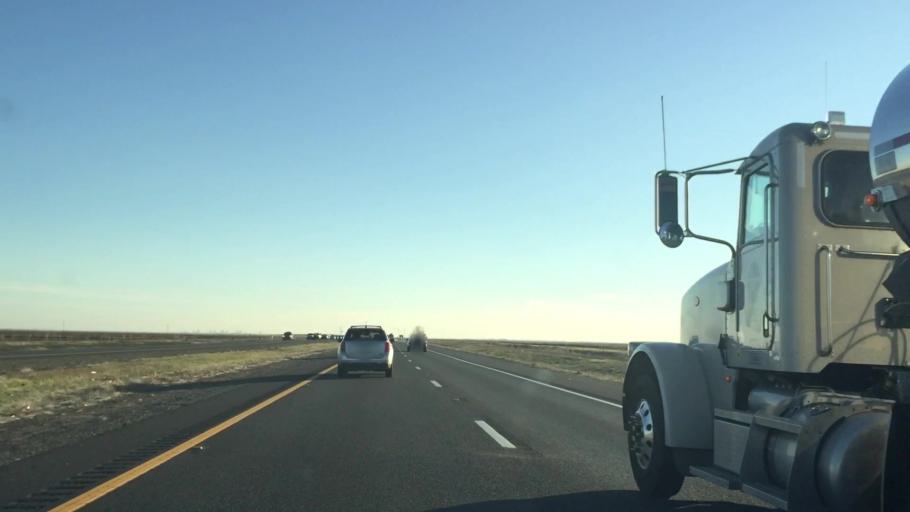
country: US
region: California
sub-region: Sacramento County
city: Elverta
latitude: 38.7877
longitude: -121.5438
